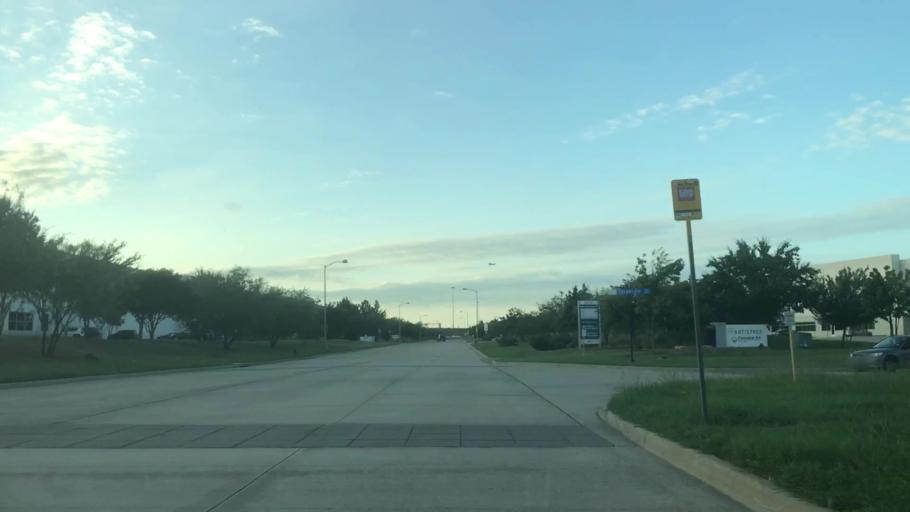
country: US
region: Texas
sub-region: Dallas County
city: Coppell
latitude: 32.9353
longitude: -97.0337
